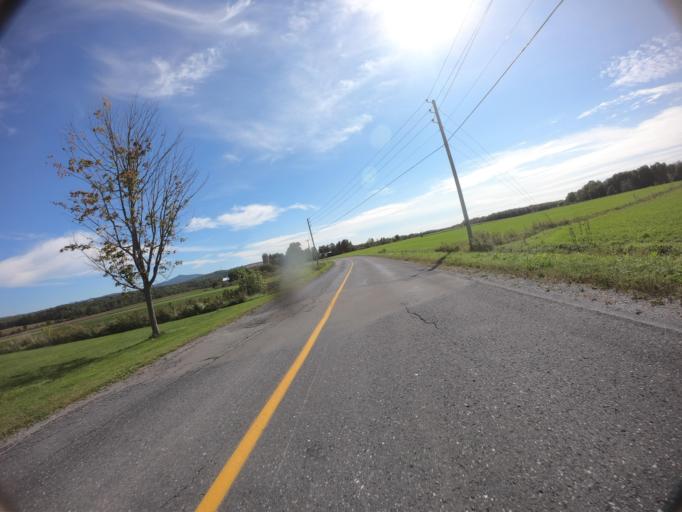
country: CA
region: Quebec
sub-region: Monteregie
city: Cowansville
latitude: 45.1571
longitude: -72.8109
